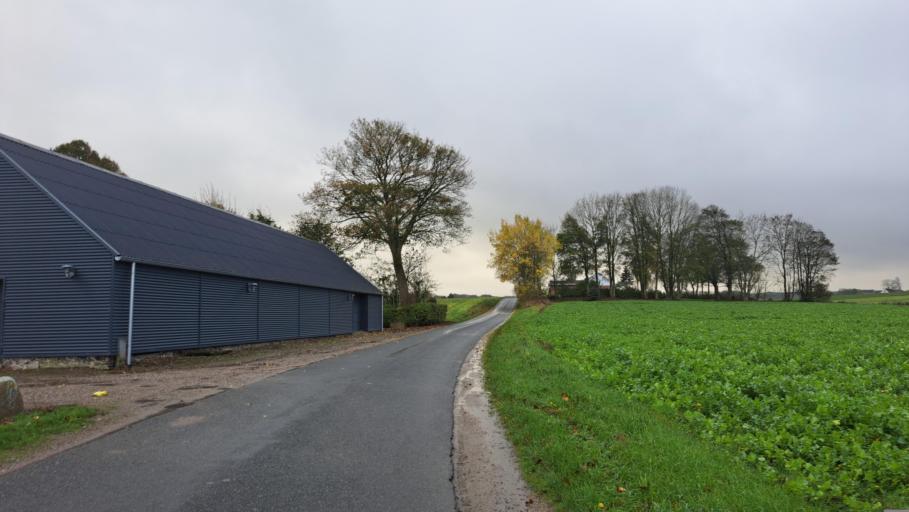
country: DK
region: Central Jutland
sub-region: Hedensted Kommune
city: Hedensted
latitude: 55.8336
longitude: 9.7356
